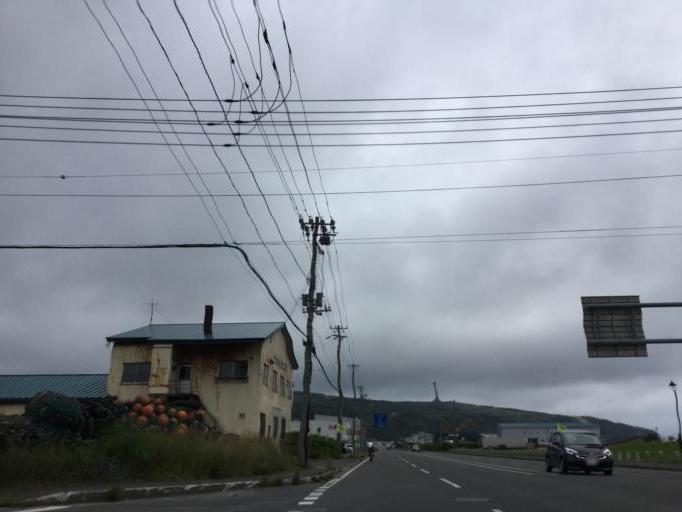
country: JP
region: Hokkaido
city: Wakkanai
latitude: 45.4016
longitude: 141.6871
